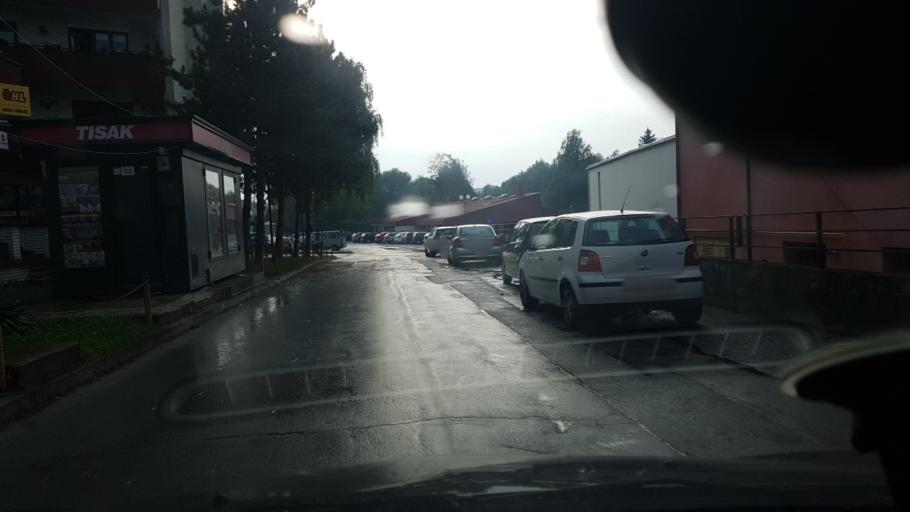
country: SI
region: Rogatec
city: Rogatec
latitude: 46.2226
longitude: 15.6996
